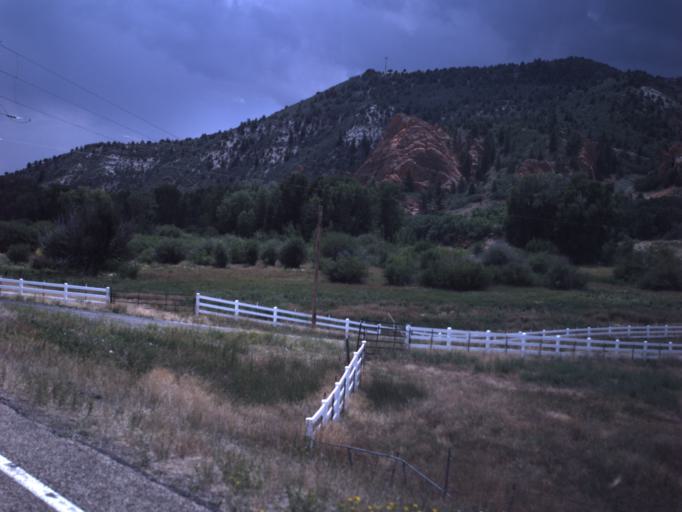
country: US
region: Utah
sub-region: Duchesne County
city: Duchesne
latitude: 40.4250
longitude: -110.7997
